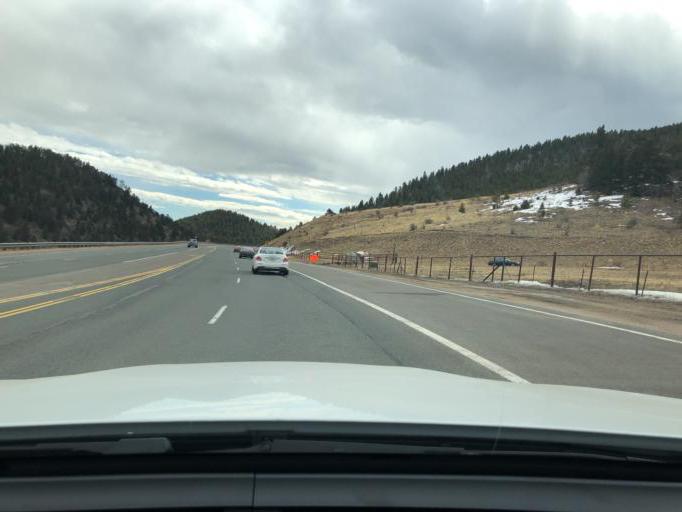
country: US
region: Colorado
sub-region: Gilpin County
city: Central City
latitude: 39.7800
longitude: -105.4807
